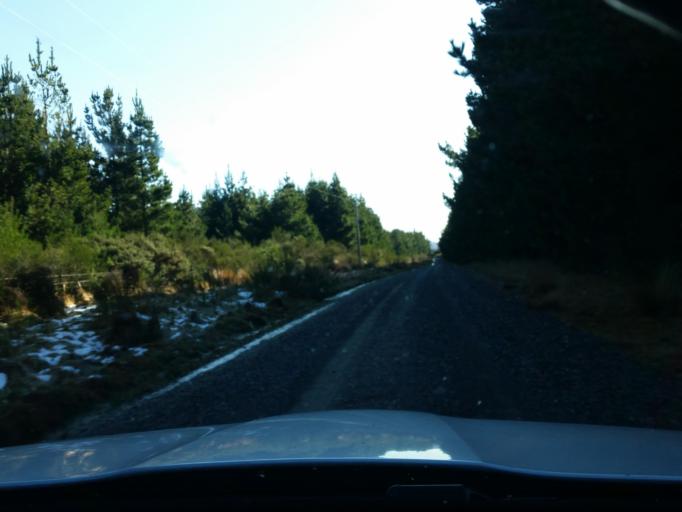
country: NZ
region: Southland
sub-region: Southland District
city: Te Anau
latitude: -45.6843
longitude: 168.1297
